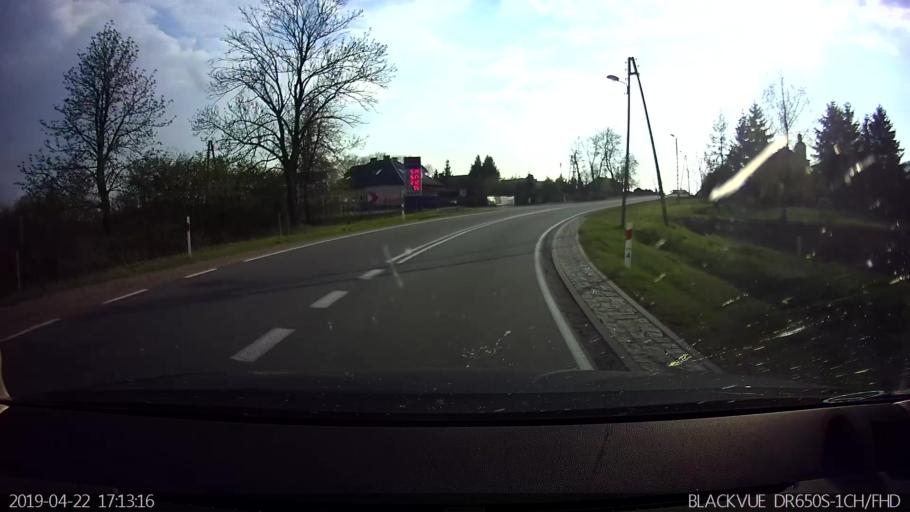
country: PL
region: Masovian Voivodeship
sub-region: Powiat siedlecki
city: Korczew
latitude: 52.4012
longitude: 22.5196
